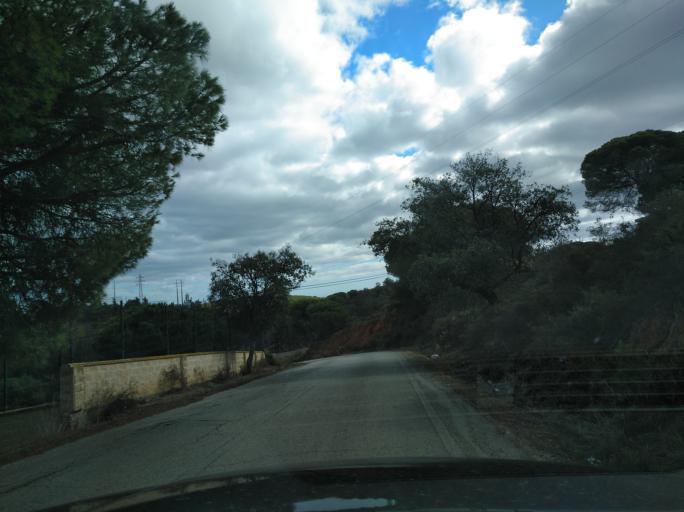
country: PT
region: Faro
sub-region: Vila Real de Santo Antonio
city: Monte Gordo
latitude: 37.1880
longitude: -7.4854
